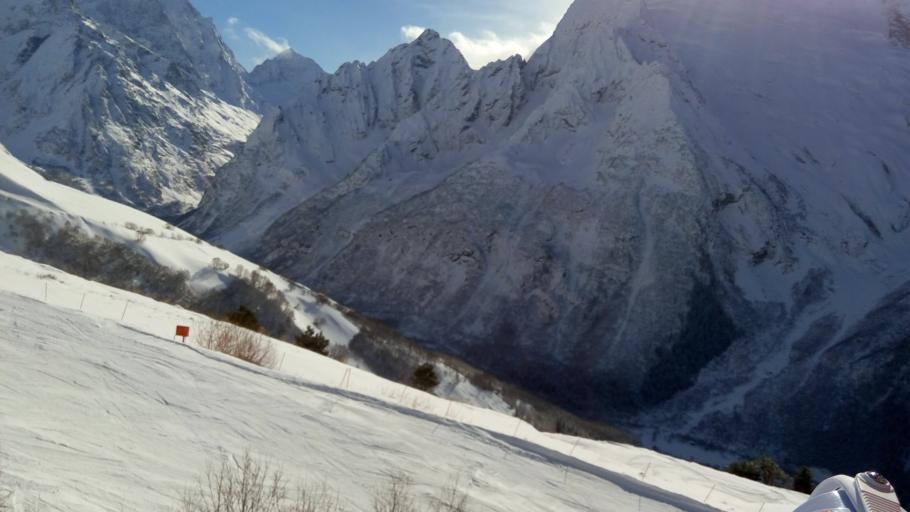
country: RU
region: Karachayevo-Cherkesiya
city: Teberda
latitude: 43.2920
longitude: 41.6494
